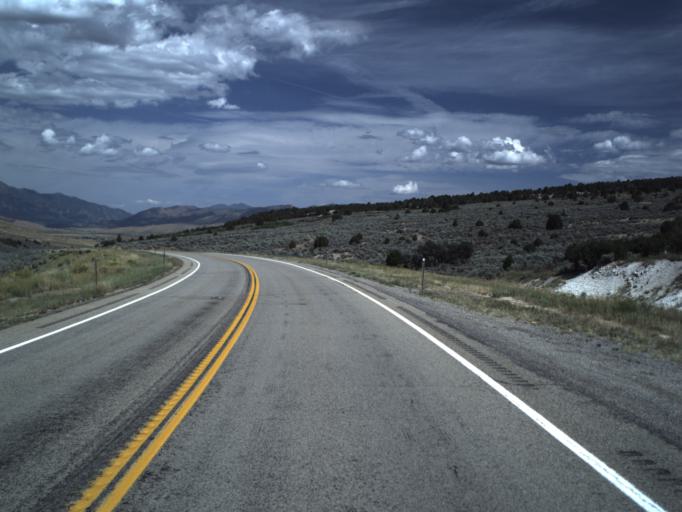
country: US
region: Utah
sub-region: Sanpete County
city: Fairview
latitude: 39.7180
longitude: -111.4708
